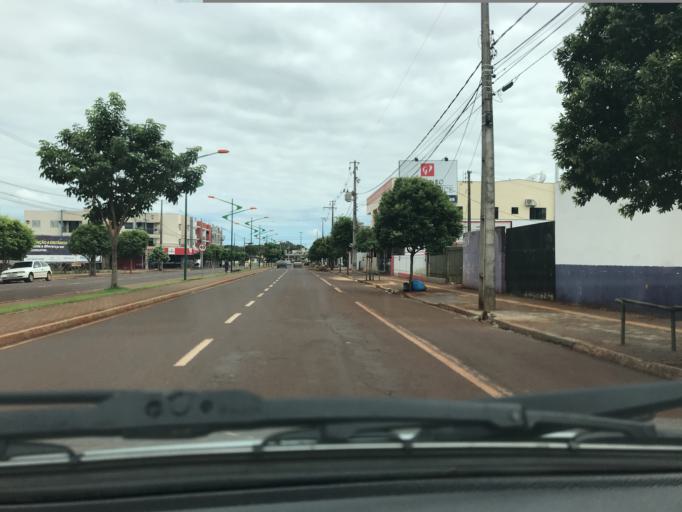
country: BR
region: Parana
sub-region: Palotina
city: Palotina
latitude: -24.2799
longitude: -53.8410
